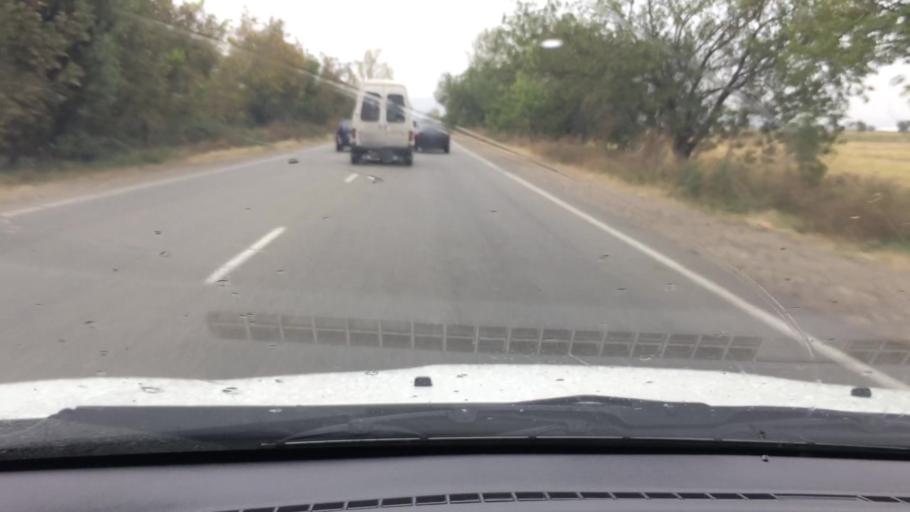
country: GE
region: Kvemo Kartli
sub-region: Marneuli
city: Marneuli
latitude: 41.5528
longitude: 44.7763
